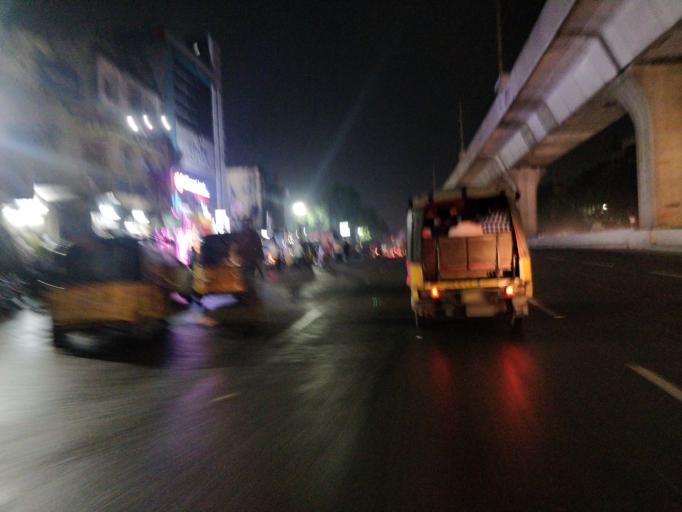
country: IN
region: Telangana
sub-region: Rangareddi
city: Gaddi Annaram
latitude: 17.3726
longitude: 78.5080
